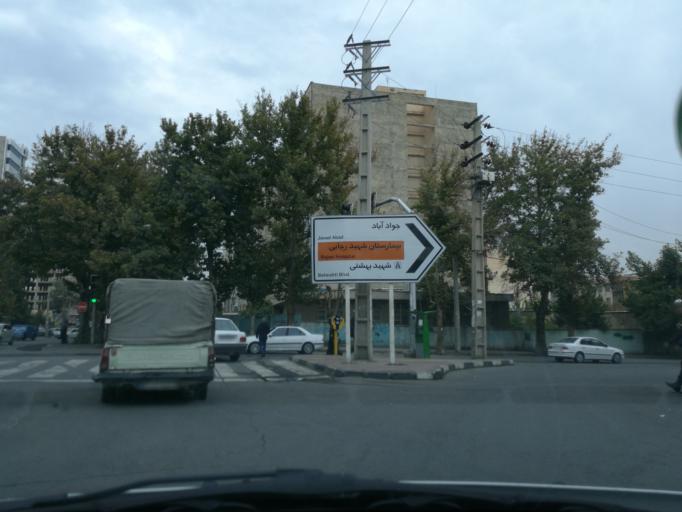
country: IR
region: Alborz
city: Karaj
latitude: 35.8561
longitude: 50.9530
